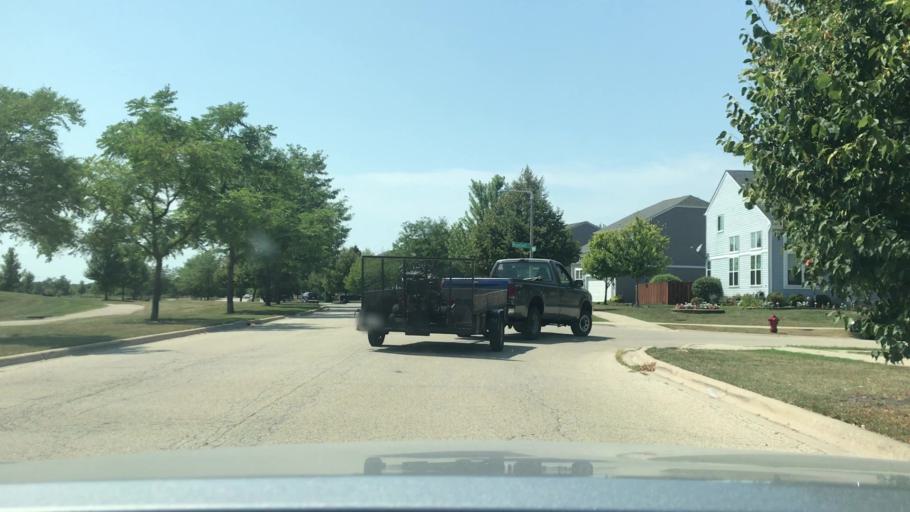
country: US
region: Illinois
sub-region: Kane County
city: Aurora
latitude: 41.7222
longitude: -88.2467
